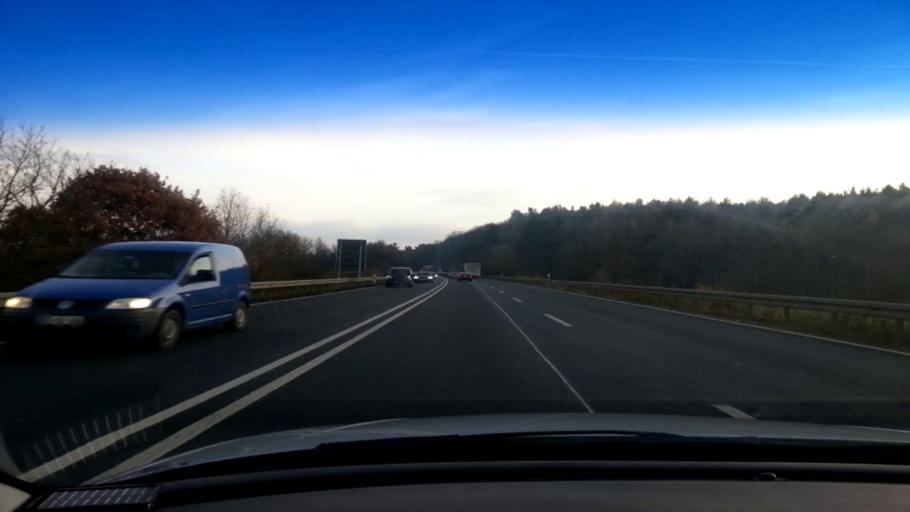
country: DE
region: Bavaria
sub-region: Upper Franconia
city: Pettstadt
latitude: 49.8266
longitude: 10.9531
